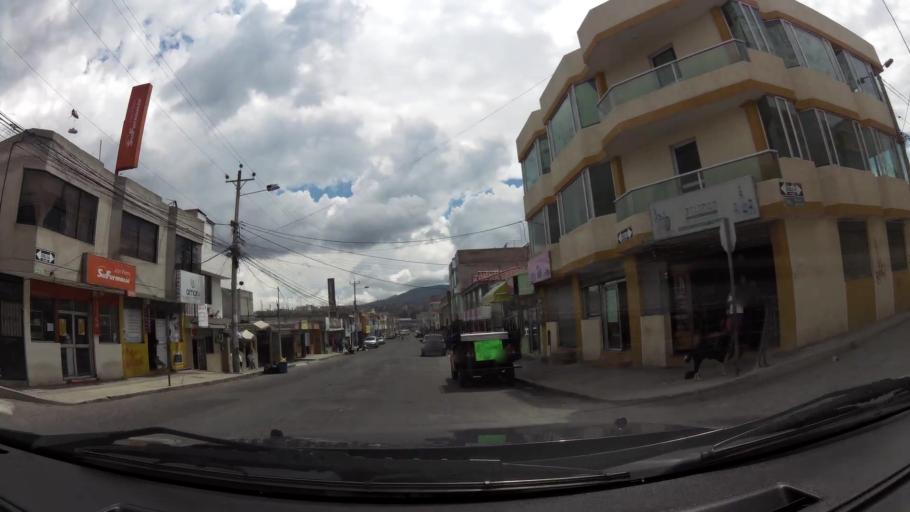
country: EC
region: Pichincha
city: Quito
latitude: -0.0804
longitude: -78.4128
